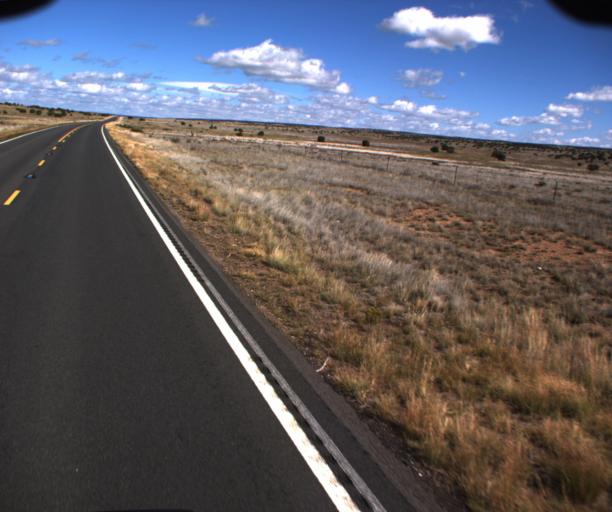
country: US
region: Arizona
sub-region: Apache County
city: Houck
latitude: 34.9316
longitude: -109.2373
